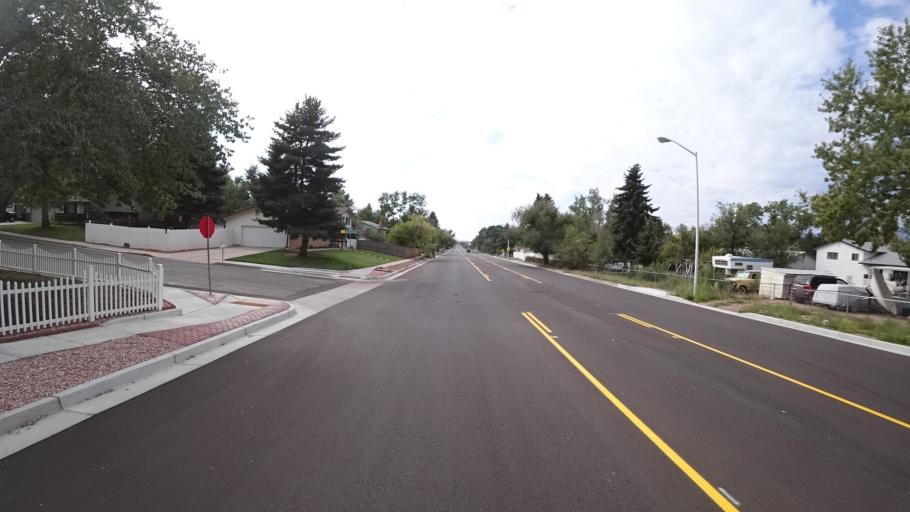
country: US
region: Colorado
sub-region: El Paso County
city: Cimarron Hills
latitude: 38.8521
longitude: -104.7294
